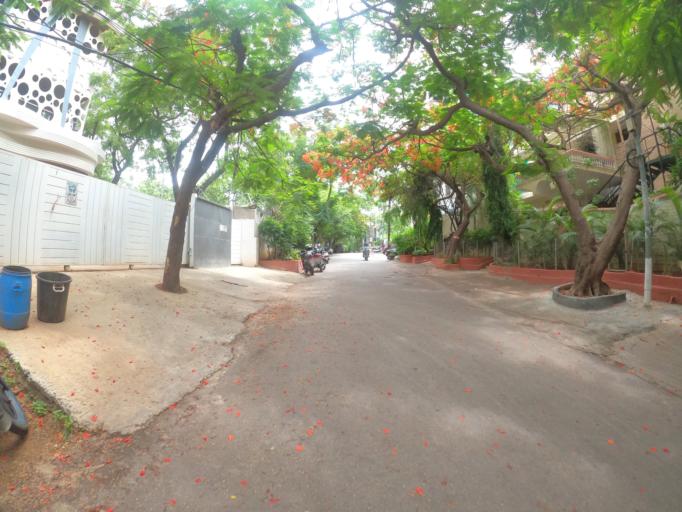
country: IN
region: Telangana
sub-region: Hyderabad
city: Hyderabad
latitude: 17.4267
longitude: 78.4484
